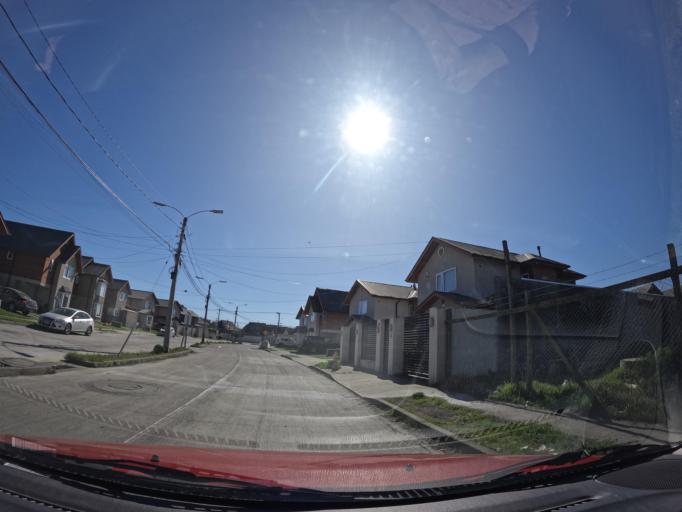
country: CL
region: Biobio
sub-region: Provincia de Concepcion
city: Concepcion
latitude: -36.8908
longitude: -73.1456
